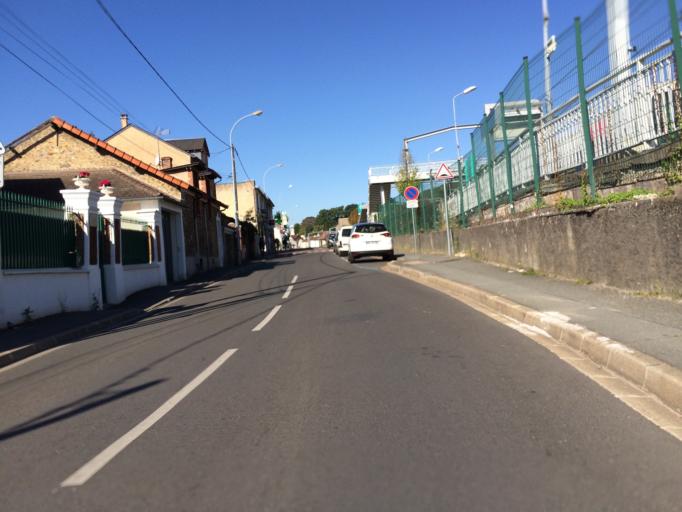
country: FR
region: Ile-de-France
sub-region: Departement de l'Essonne
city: Villebon-sur-Yvette
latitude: 48.7055
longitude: 2.2134
